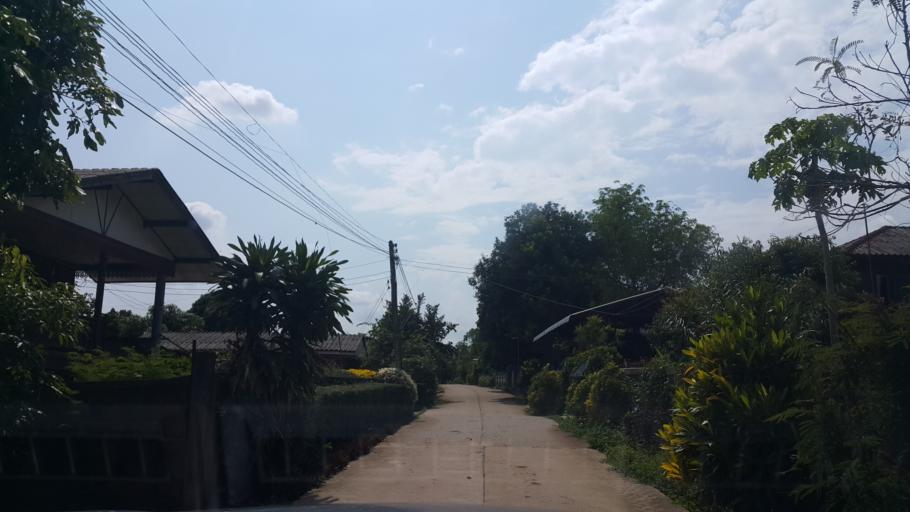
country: TH
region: Chiang Rai
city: Wiang Chiang Rung
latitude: 20.0203
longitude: 99.9332
